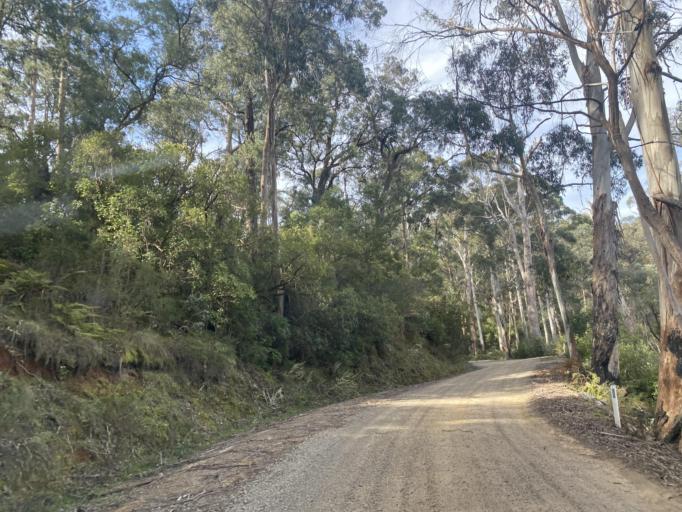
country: AU
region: Victoria
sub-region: Mansfield
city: Mansfield
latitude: -36.8444
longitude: 146.1719
